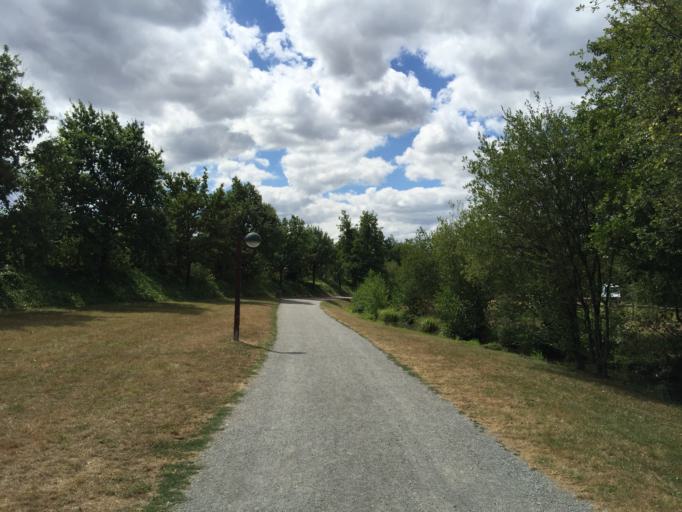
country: FR
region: Rhone-Alpes
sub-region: Departement de la Loire
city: Savigneux
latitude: 45.6108
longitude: 4.0902
